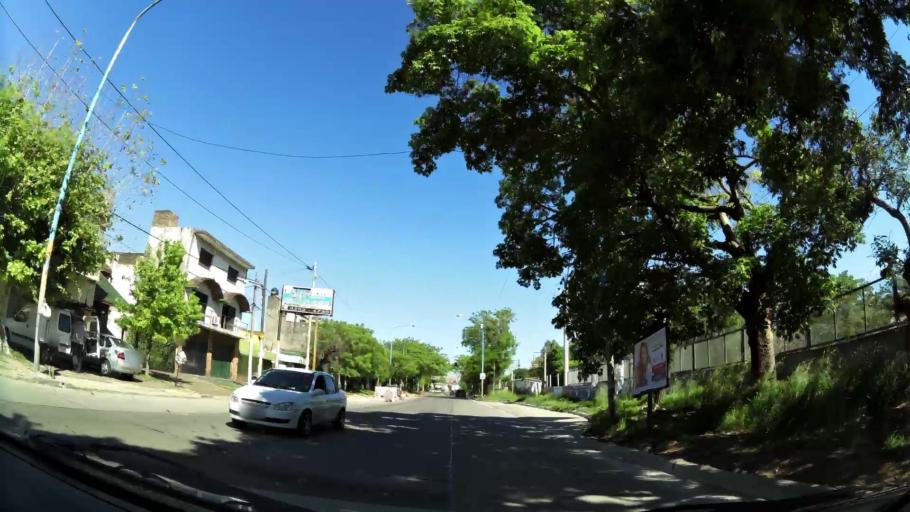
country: AR
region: Buenos Aires
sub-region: Partido de Quilmes
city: Quilmes
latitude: -34.7021
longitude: -58.3006
